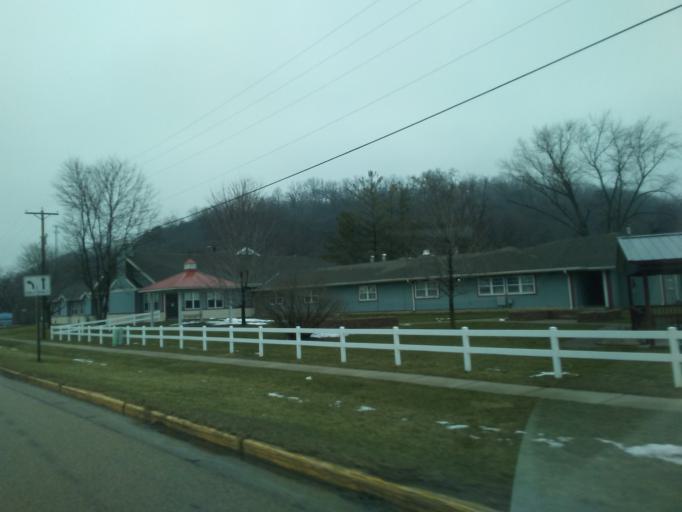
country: US
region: Wisconsin
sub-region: Dane County
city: Black Earth
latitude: 43.1428
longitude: -89.7470
